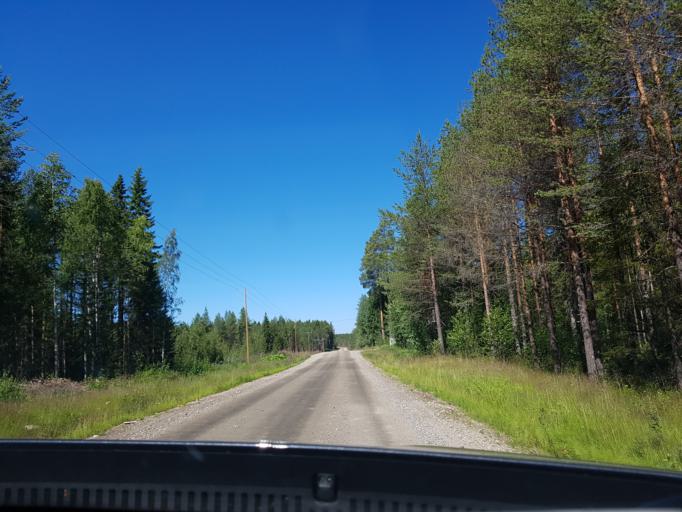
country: FI
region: Kainuu
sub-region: Kehys-Kainuu
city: Kuhmo
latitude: 64.1780
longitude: 29.6083
